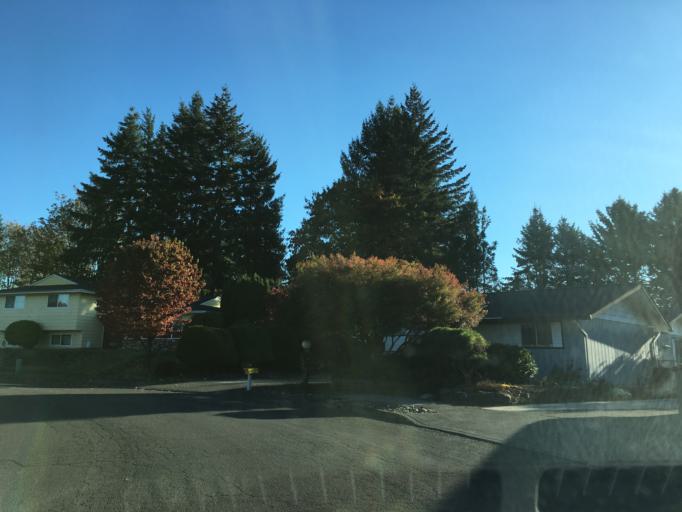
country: US
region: Oregon
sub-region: Multnomah County
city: Wood Village
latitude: 45.5123
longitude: -122.4128
